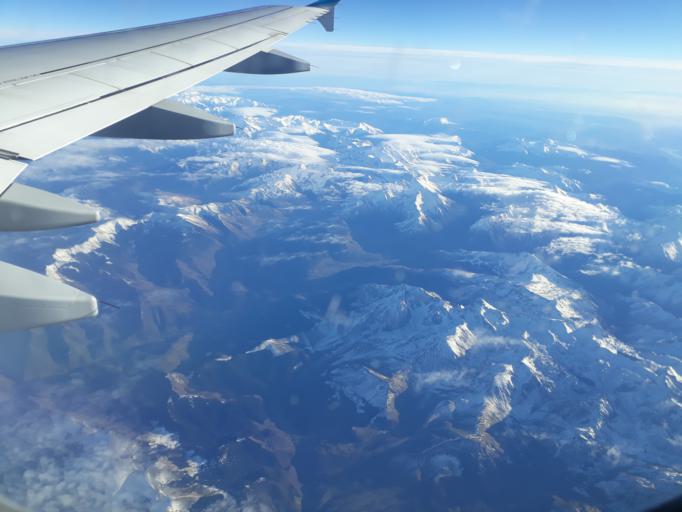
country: FR
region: Midi-Pyrenees
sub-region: Departement des Hautes-Pyrenees
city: Campan
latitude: 43.0312
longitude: 0.1933
